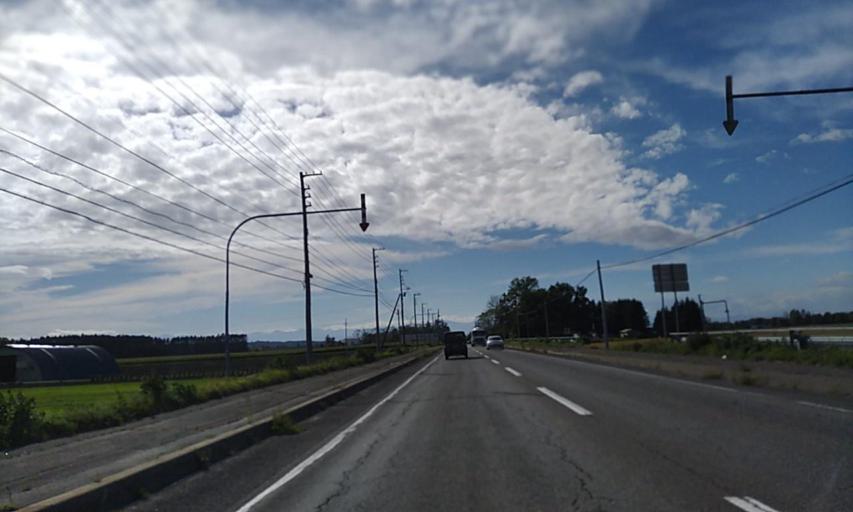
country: JP
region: Hokkaido
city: Obihiro
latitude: 42.9199
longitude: 143.3225
